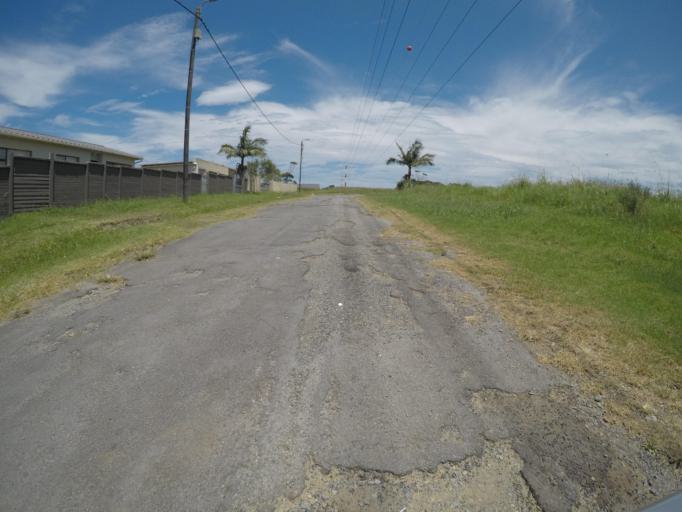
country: ZA
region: Eastern Cape
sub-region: Buffalo City Metropolitan Municipality
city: East London
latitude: -33.0326
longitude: 27.8480
